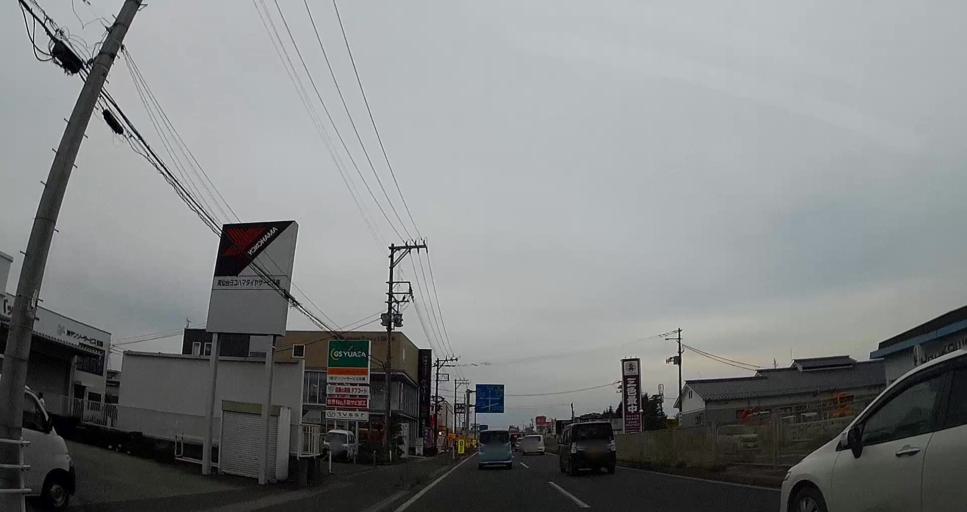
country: JP
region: Miyagi
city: Iwanuma
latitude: 38.1695
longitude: 140.8900
